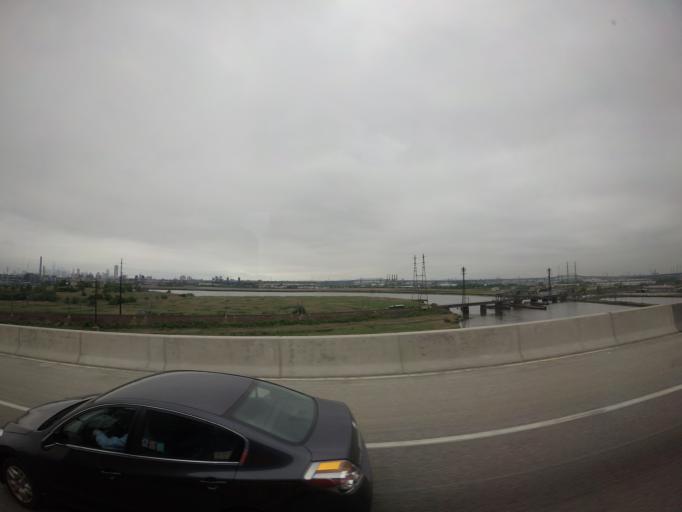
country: US
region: New Jersey
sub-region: Hudson County
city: Jersey City
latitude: 40.7571
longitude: -74.0921
